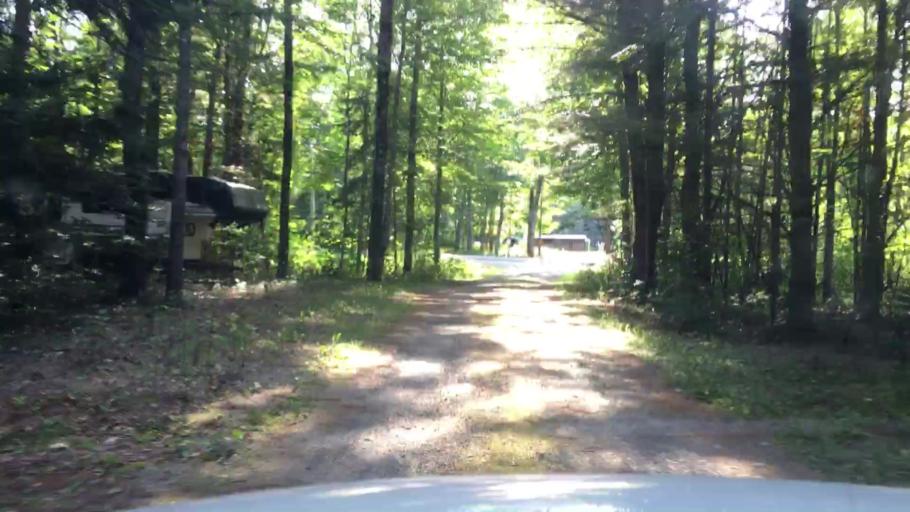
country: US
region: Maine
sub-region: Penobscot County
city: Enfield
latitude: 45.2338
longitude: -68.5429
